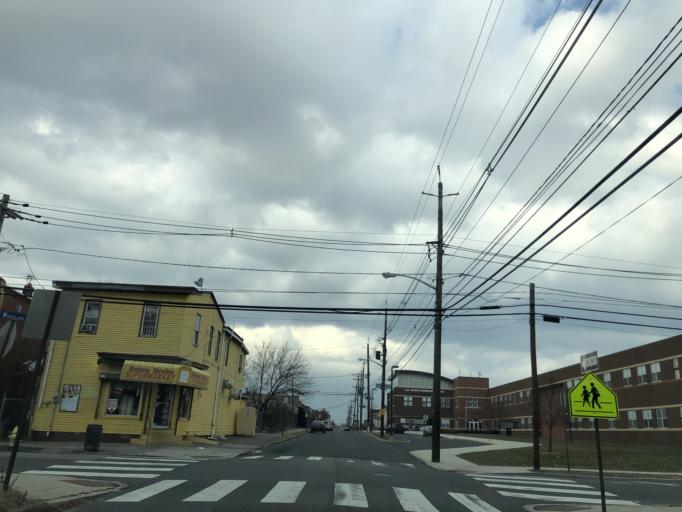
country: US
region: New Jersey
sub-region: Camden County
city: Camden
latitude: 39.9153
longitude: -75.1123
